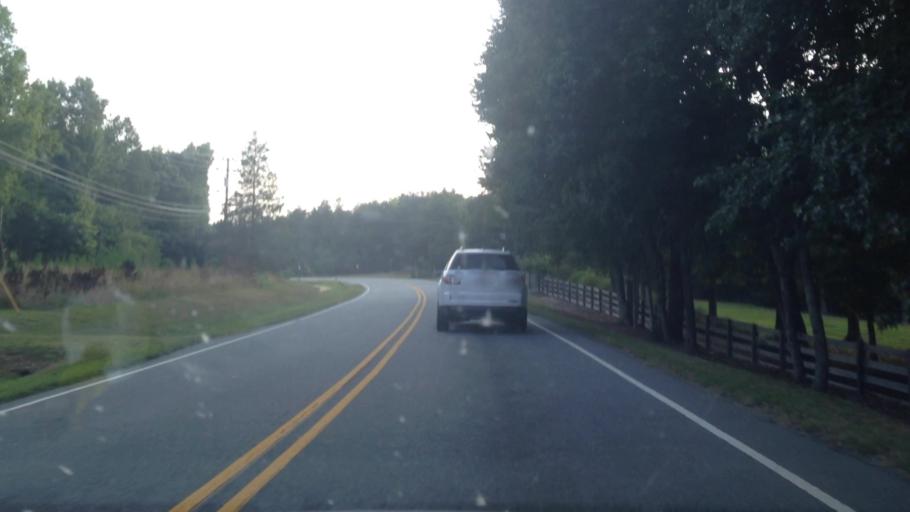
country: US
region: North Carolina
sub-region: Davidson County
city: Wallburg
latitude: 35.9725
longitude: -80.0832
